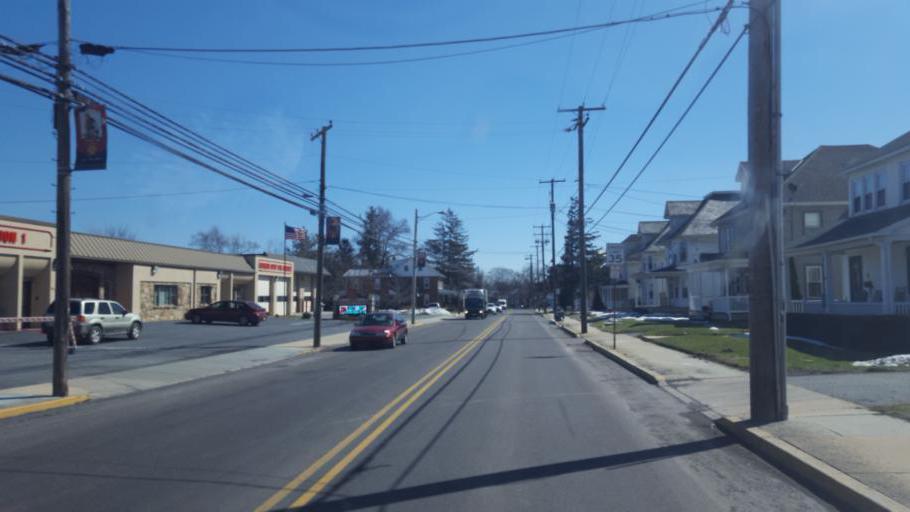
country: US
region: Pennsylvania
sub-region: Lancaster County
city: New Holland
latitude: 40.1041
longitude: -76.0825
